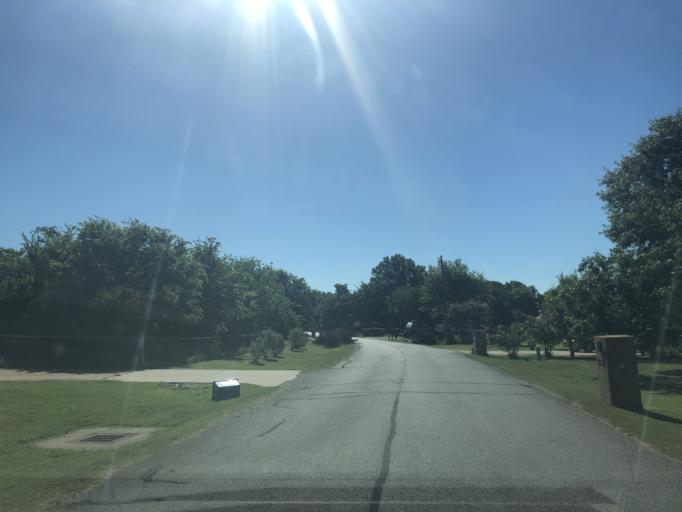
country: US
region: Texas
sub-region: Dallas County
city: Duncanville
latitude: 32.6529
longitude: -96.9407
